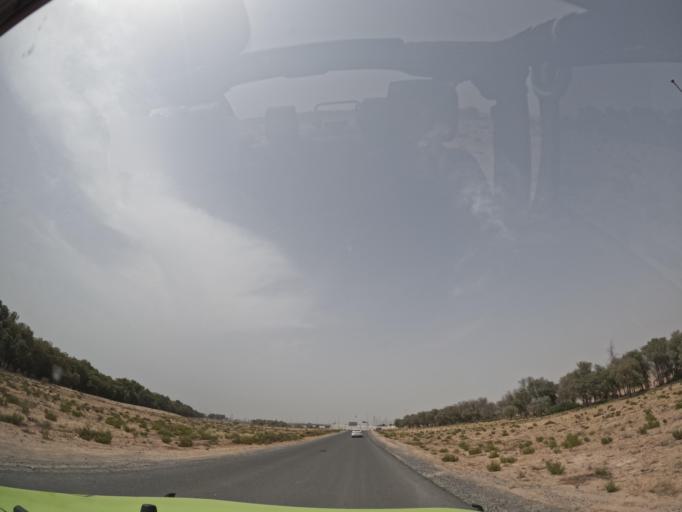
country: AE
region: Dubai
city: Dubai
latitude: 25.1447
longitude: 55.3408
